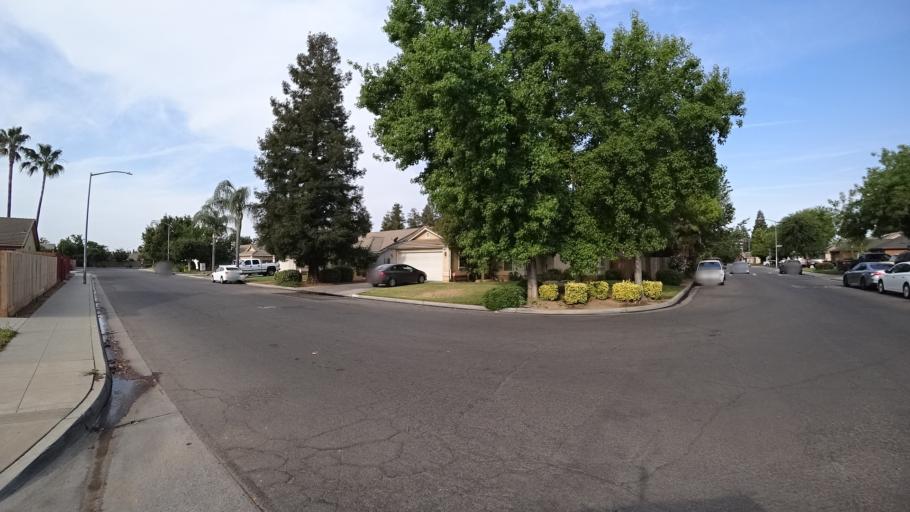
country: US
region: California
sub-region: Fresno County
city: West Park
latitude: 36.7730
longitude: -119.8654
